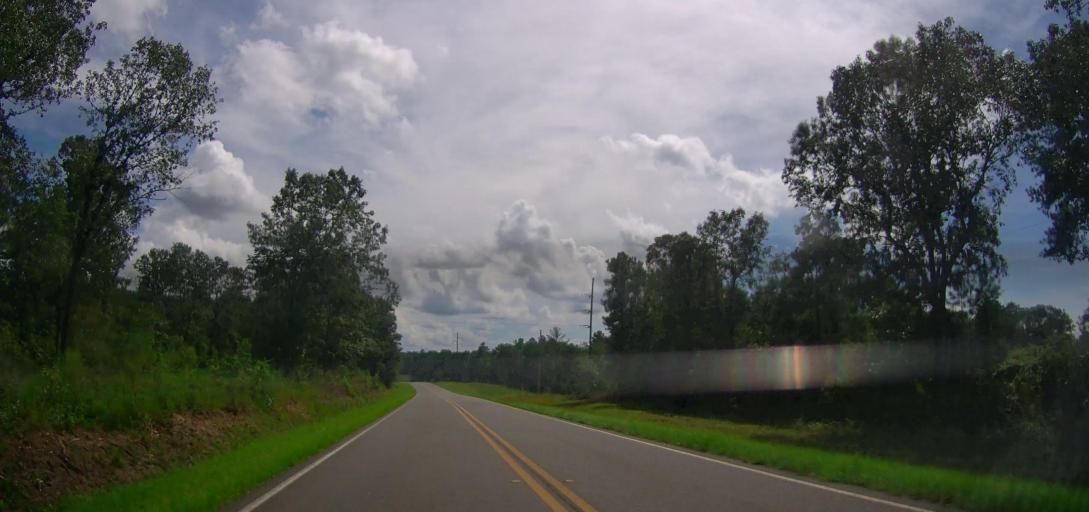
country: US
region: Georgia
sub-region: Taylor County
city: Butler
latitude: 32.5161
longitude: -84.2049
